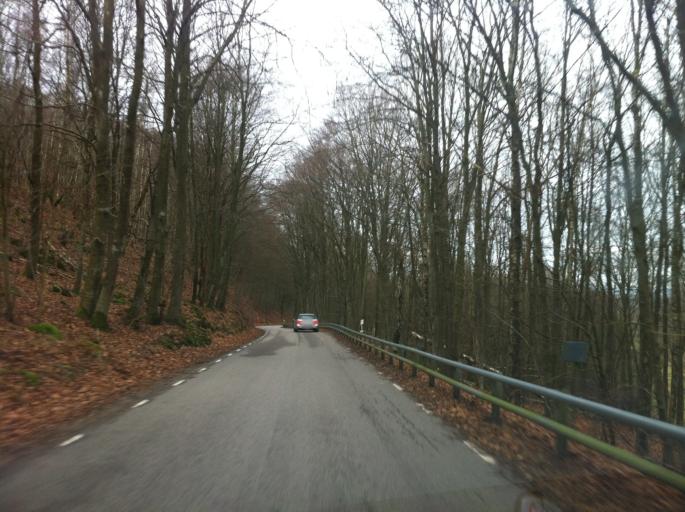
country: SE
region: Skane
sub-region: Astorps Kommun
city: Kvidinge
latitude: 56.0857
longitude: 13.0966
